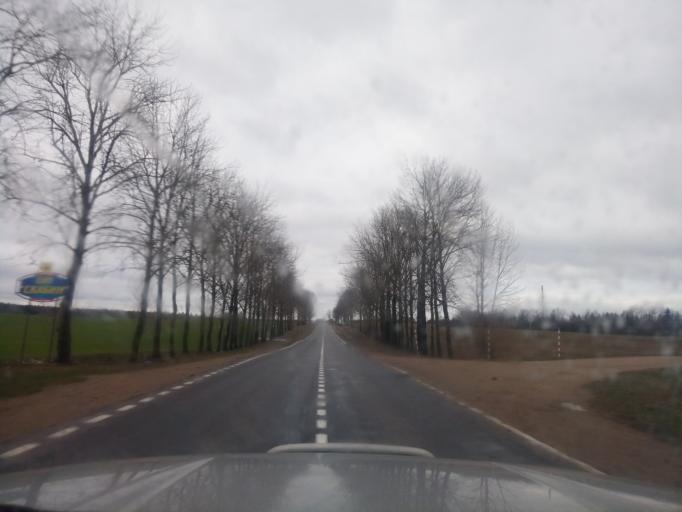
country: BY
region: Minsk
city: Kapyl'
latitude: 53.1706
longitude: 27.1383
